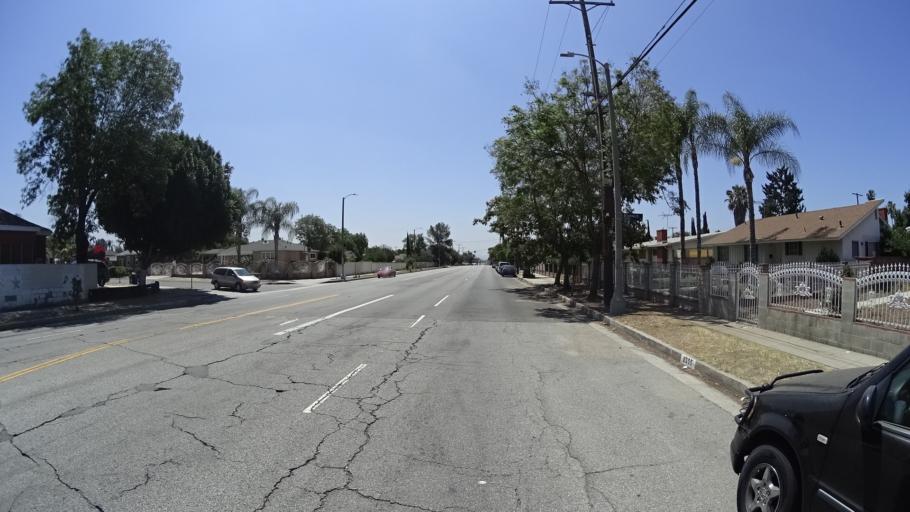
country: US
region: California
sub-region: Los Angeles County
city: San Fernando
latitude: 34.2403
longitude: -118.4243
